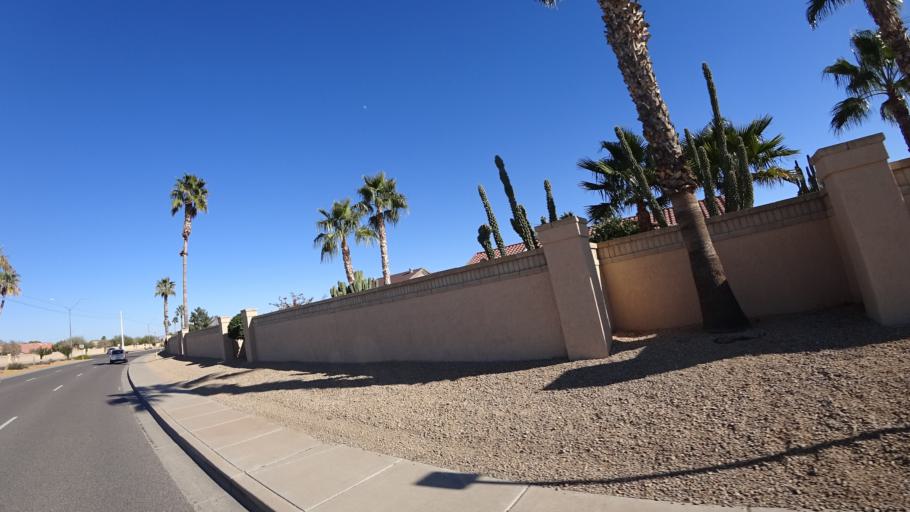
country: US
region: Arizona
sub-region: Maricopa County
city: Sun City West
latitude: 33.6712
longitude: -112.3885
